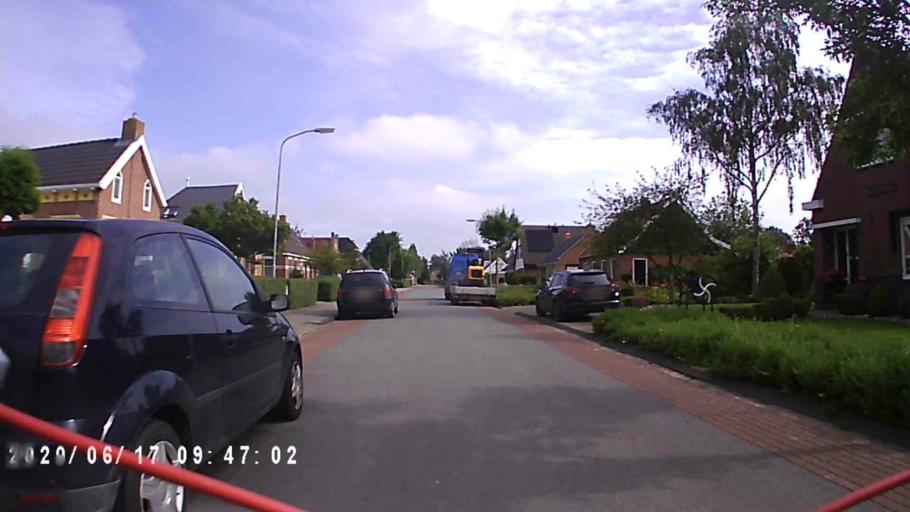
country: NL
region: Groningen
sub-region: Gemeente De Marne
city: Ulrum
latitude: 53.3573
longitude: 6.3382
